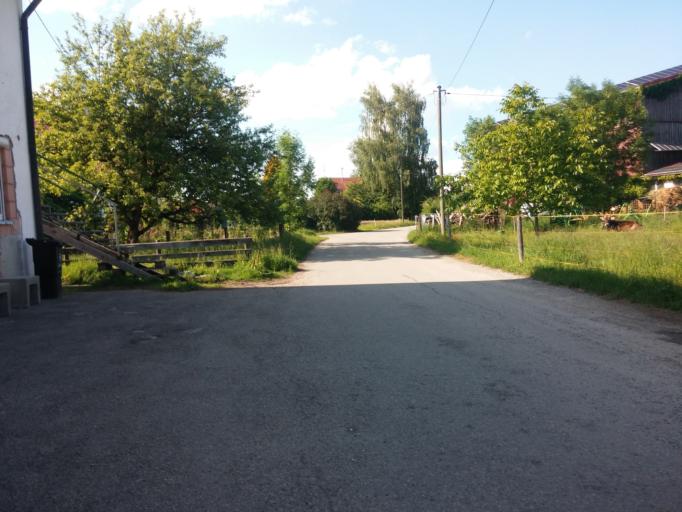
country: DE
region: Bavaria
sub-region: Swabia
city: Woringen
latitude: 47.8818
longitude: 10.1958
